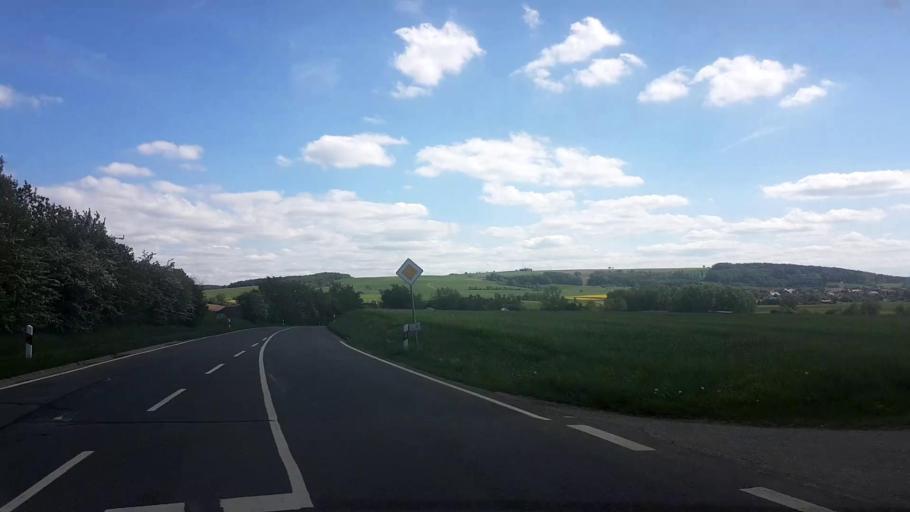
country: DE
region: Bavaria
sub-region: Regierungsbezirk Unterfranken
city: Untermerzbach
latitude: 50.1362
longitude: 10.8824
